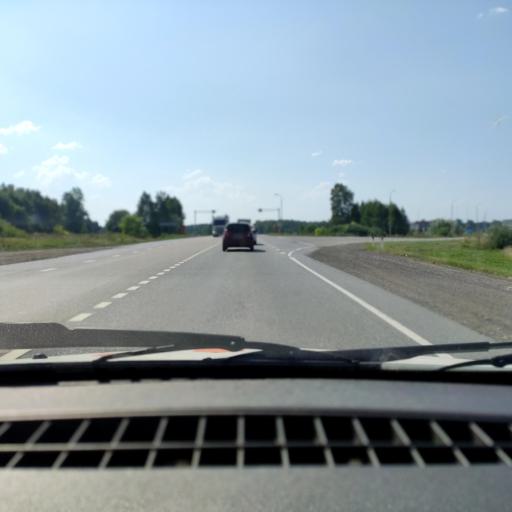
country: RU
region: Bashkortostan
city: Iglino
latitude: 54.7811
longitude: 56.5099
